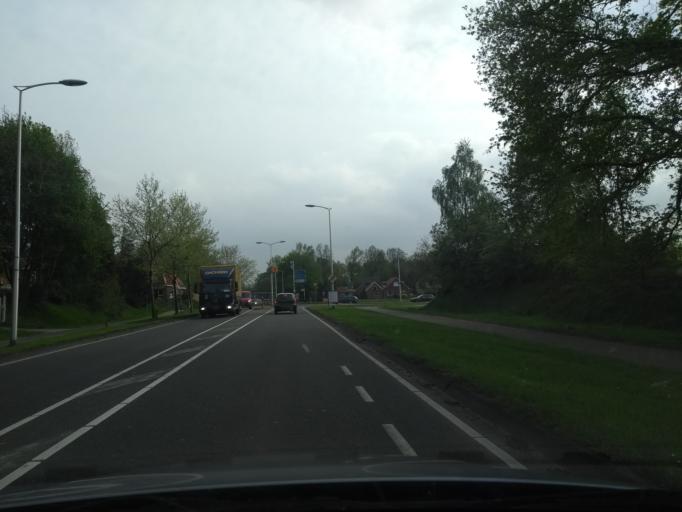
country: NL
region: Overijssel
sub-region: Gemeente Oldenzaal
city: Oldenzaal
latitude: 52.3232
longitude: 6.9338
